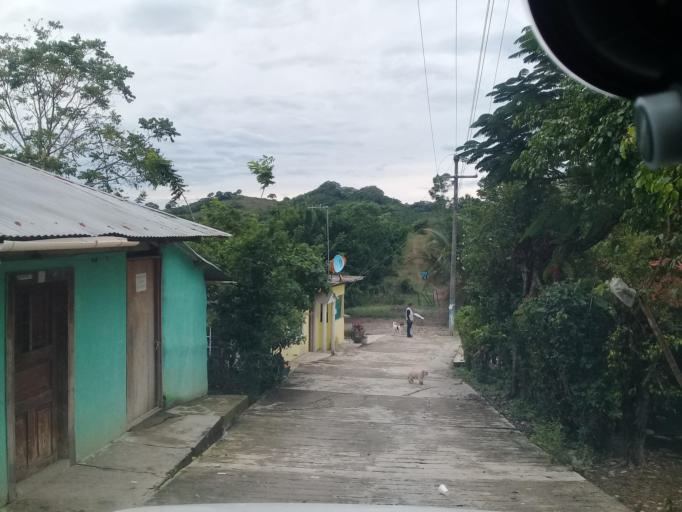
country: MX
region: Veracruz
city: Platon Sanchez
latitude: 21.2165
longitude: -98.3742
